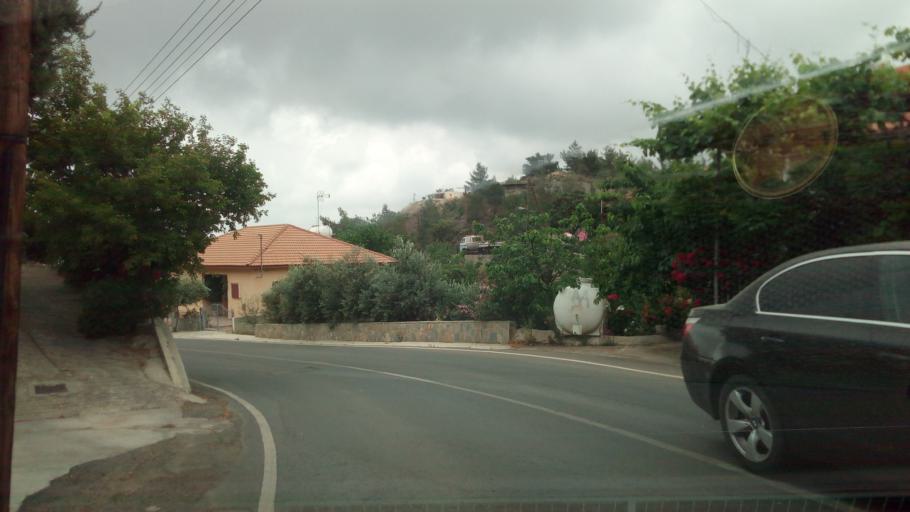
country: CY
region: Limassol
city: Pelendri
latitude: 34.8496
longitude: 33.0245
